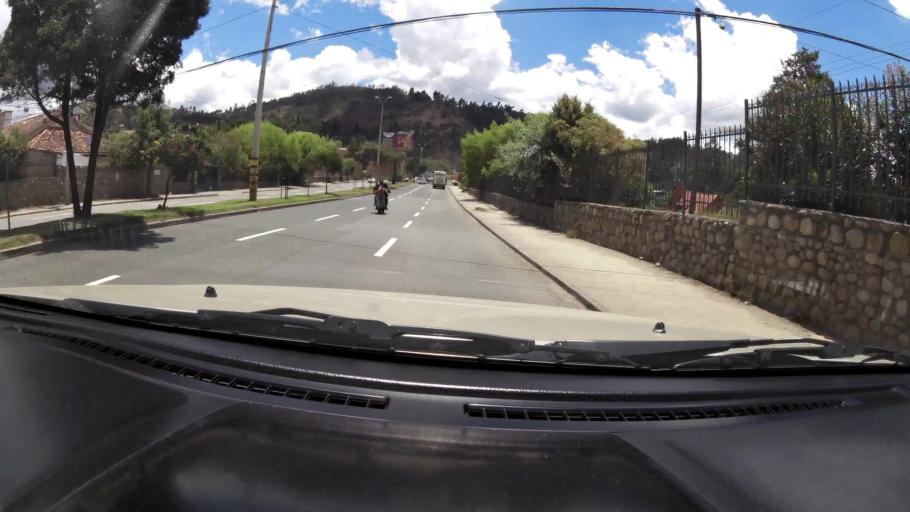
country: EC
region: Azuay
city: Cuenca
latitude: -2.8908
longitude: -78.9635
